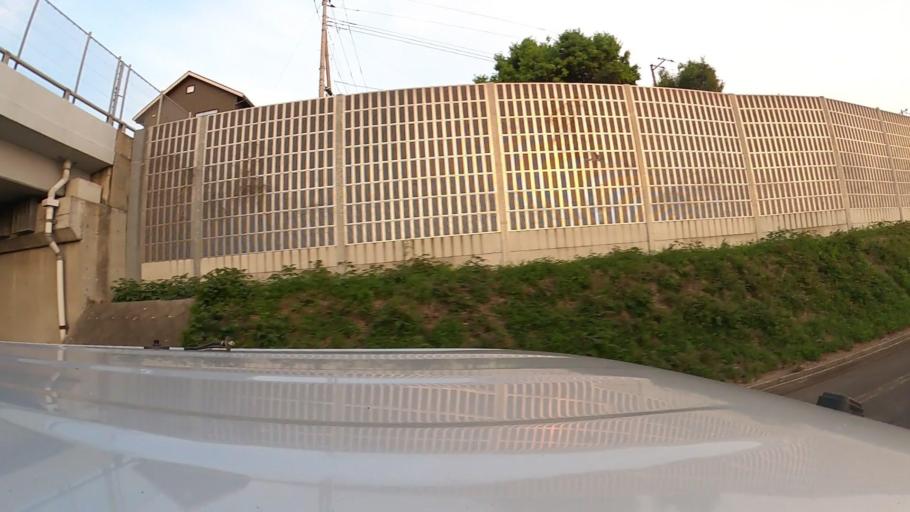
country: JP
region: Ibaraki
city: Mitsukaido
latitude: 36.0019
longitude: 140.0388
